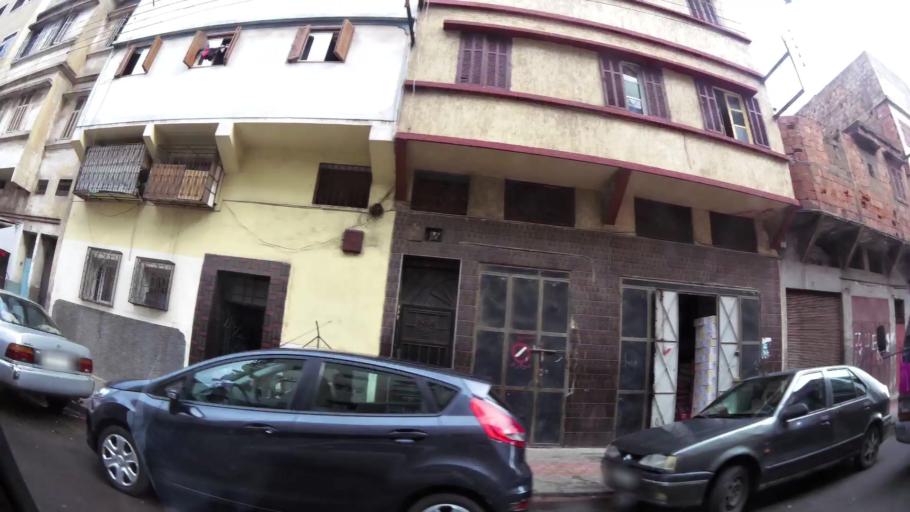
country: MA
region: Grand Casablanca
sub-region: Casablanca
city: Casablanca
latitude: 33.5460
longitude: -7.5749
